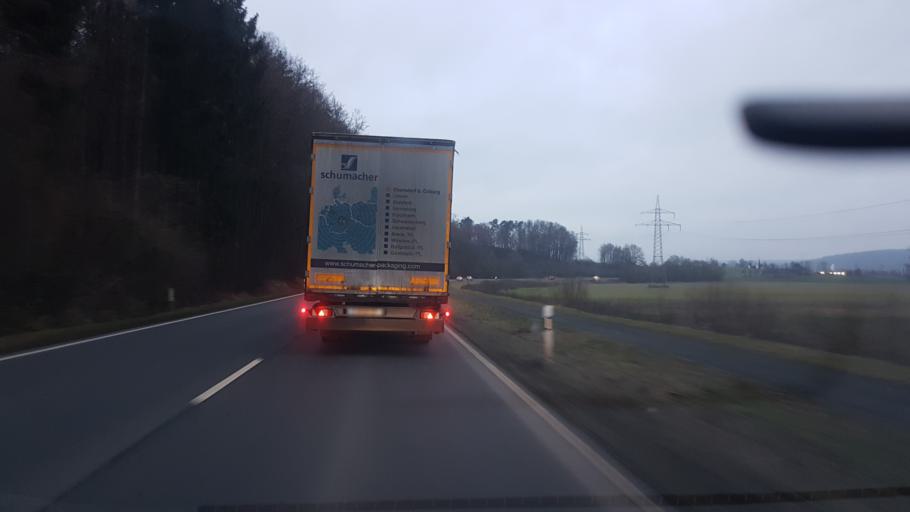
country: DE
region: Bavaria
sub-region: Regierungsbezirk Unterfranken
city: Rentweinsdorf
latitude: 50.0719
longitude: 10.7940
